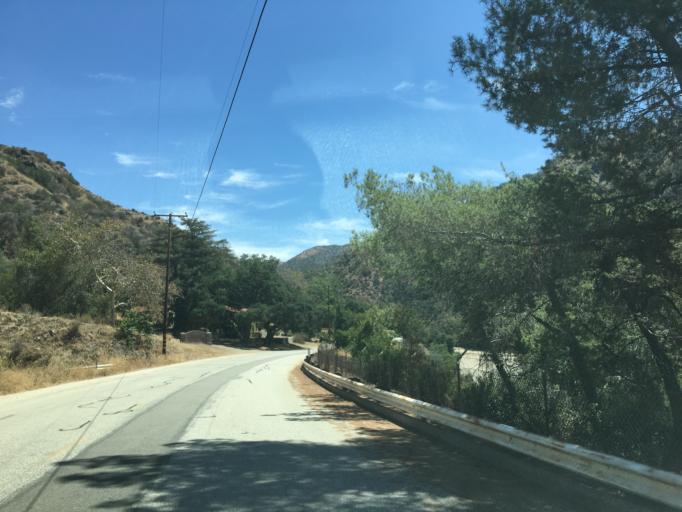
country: US
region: California
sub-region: Los Angeles County
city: Glendora
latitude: 34.1571
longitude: -117.8330
